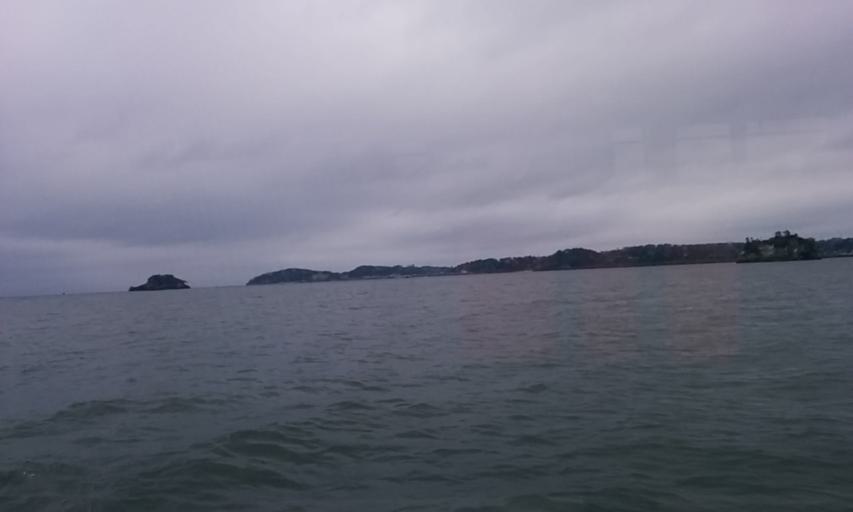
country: JP
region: Miyagi
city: Matsushima
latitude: 38.3283
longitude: 141.0834
